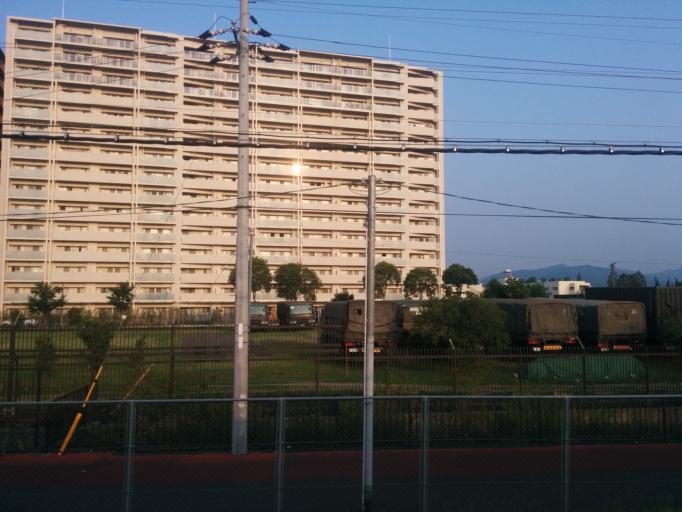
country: JP
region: Kyoto
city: Muko
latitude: 34.9653
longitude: 135.7104
